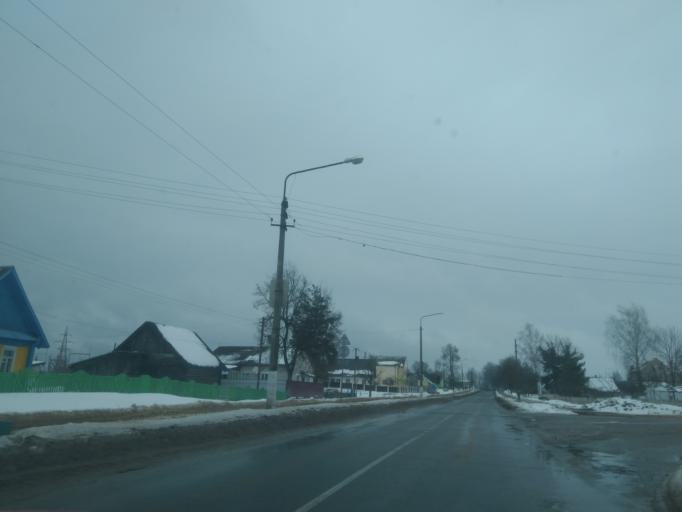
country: BY
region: Minsk
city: Ivyanyets
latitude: 53.8966
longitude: 26.7463
